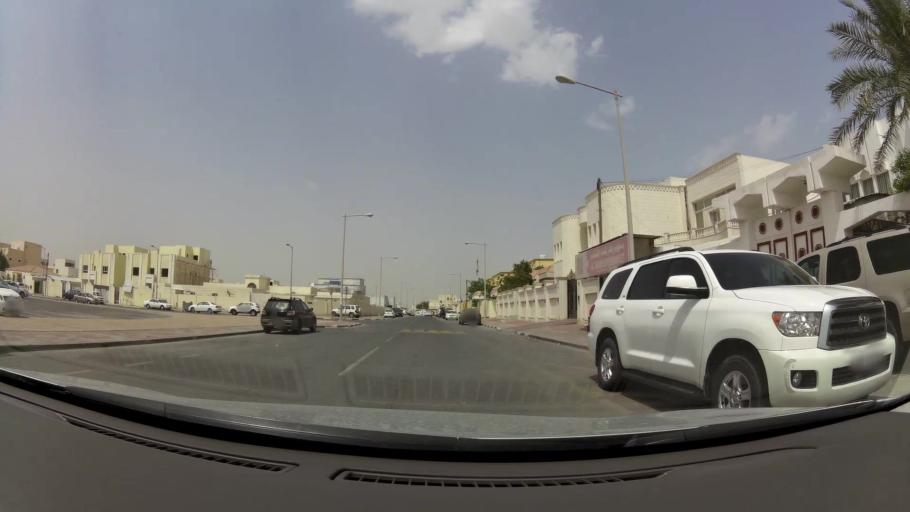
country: QA
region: Baladiyat ar Rayyan
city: Ar Rayyan
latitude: 25.2328
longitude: 51.4300
